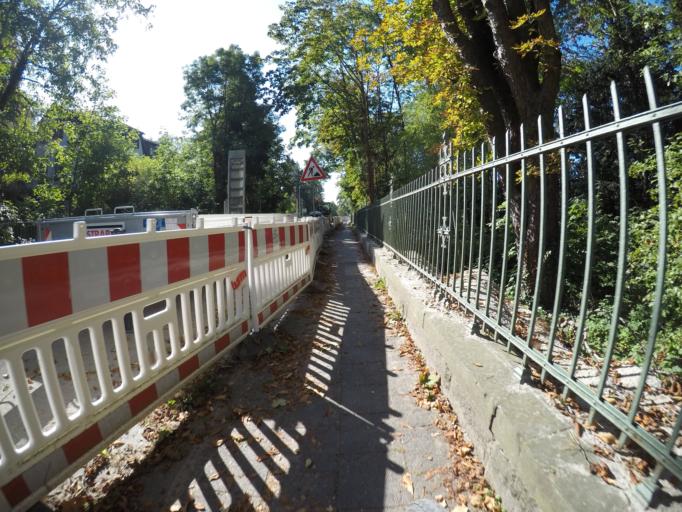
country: DE
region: Hesse
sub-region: Regierungsbezirk Darmstadt
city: Riedstadt
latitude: 49.8205
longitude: 8.5026
